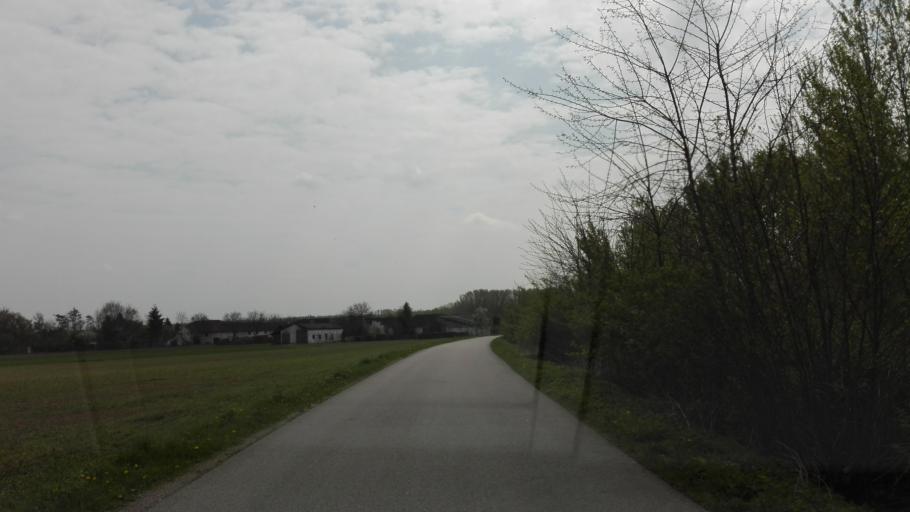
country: AT
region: Lower Austria
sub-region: Politischer Bezirk Amstetten
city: Strengberg
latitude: 48.1858
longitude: 14.6458
